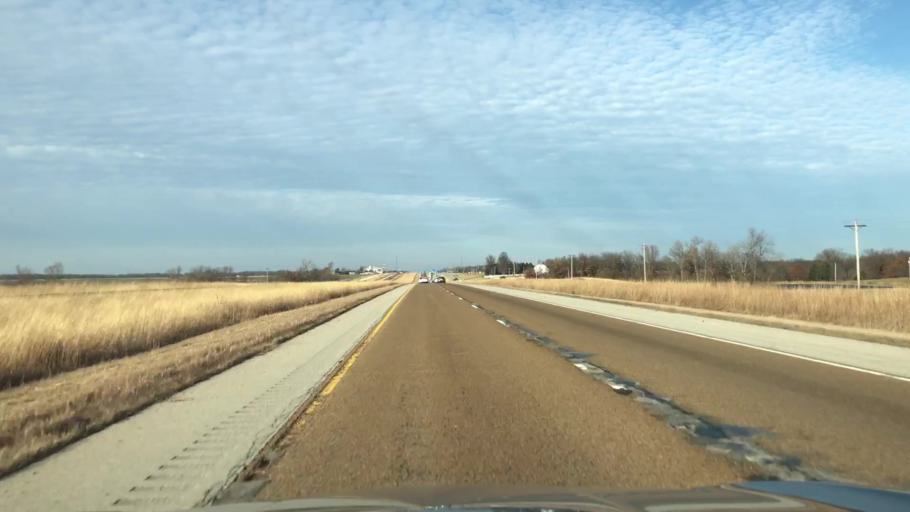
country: US
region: Illinois
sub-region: Montgomery County
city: Litchfield
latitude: 39.2445
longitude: -89.6412
